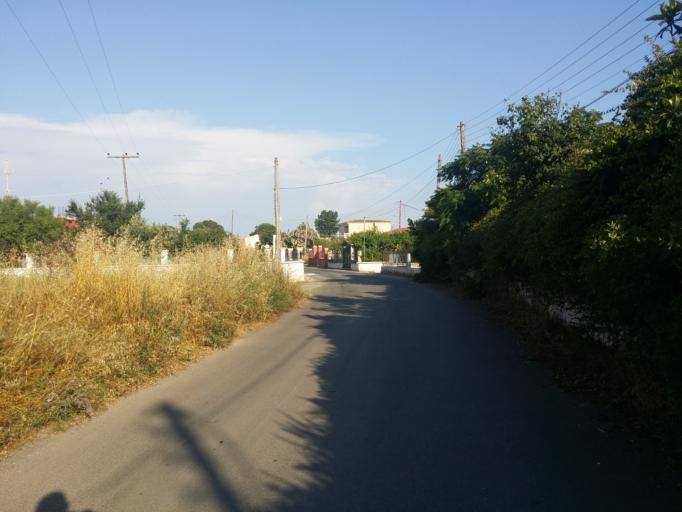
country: GR
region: Ionian Islands
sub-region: Nomos Kerkyras
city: Perivoli
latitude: 39.4289
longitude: 19.9455
